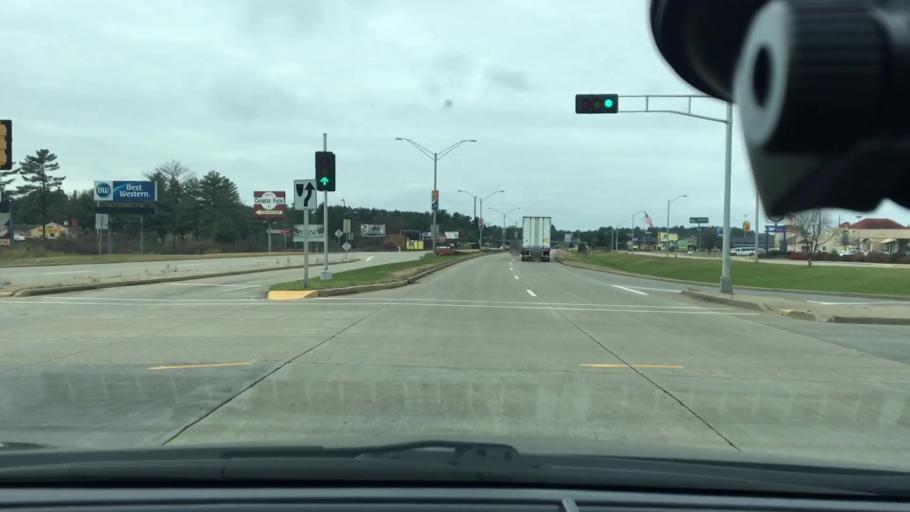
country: US
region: Wisconsin
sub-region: Columbia County
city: Wisconsin Dells
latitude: 43.6242
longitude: -89.7937
